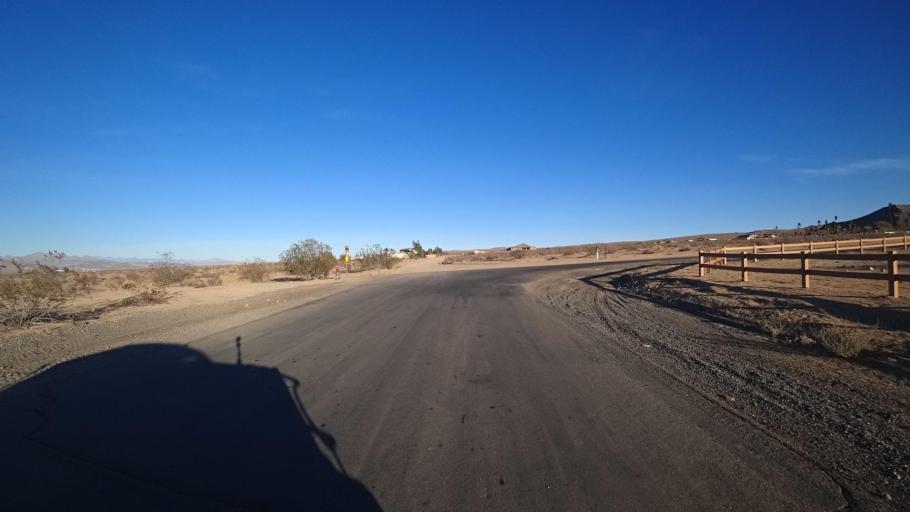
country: US
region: California
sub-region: Kern County
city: Ridgecrest
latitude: 35.5860
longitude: -117.6485
